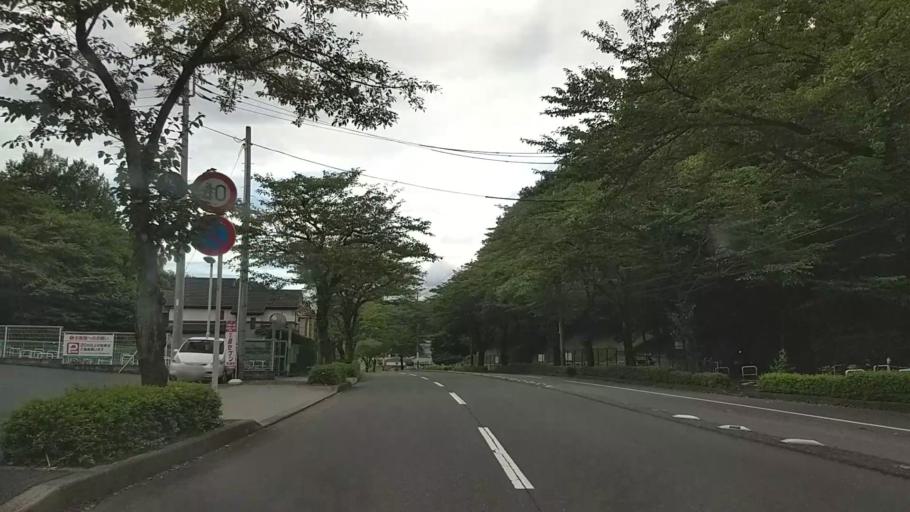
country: JP
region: Tokyo
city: Hachioji
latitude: 35.6142
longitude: 139.2965
